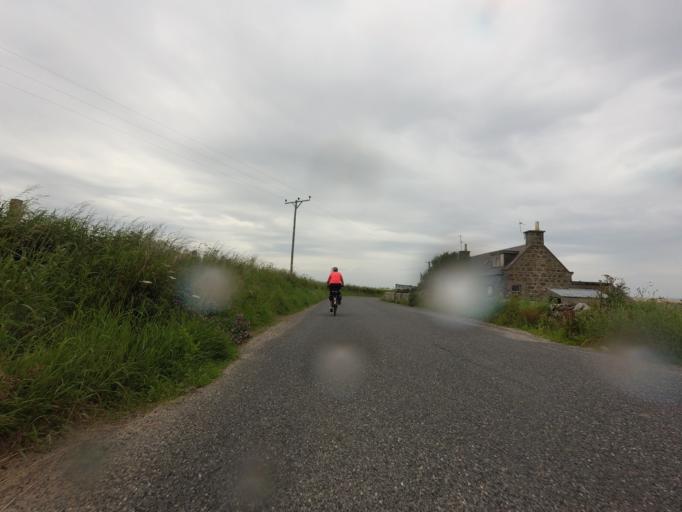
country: GB
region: Scotland
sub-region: Aberdeenshire
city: Portsoy
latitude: 57.6732
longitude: -2.6405
